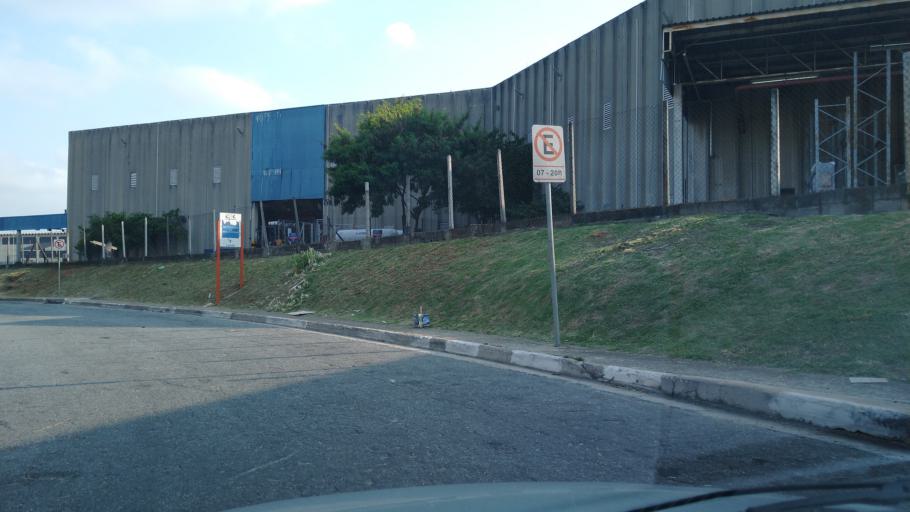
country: BR
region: Sao Paulo
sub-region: Guarulhos
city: Guarulhos
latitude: -23.4885
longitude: -46.5427
